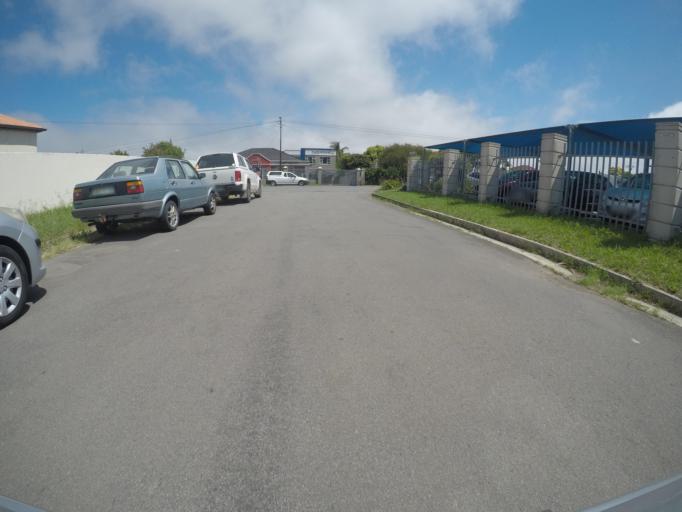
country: ZA
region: Eastern Cape
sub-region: Buffalo City Metropolitan Municipality
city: East London
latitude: -32.9776
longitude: 27.9013
